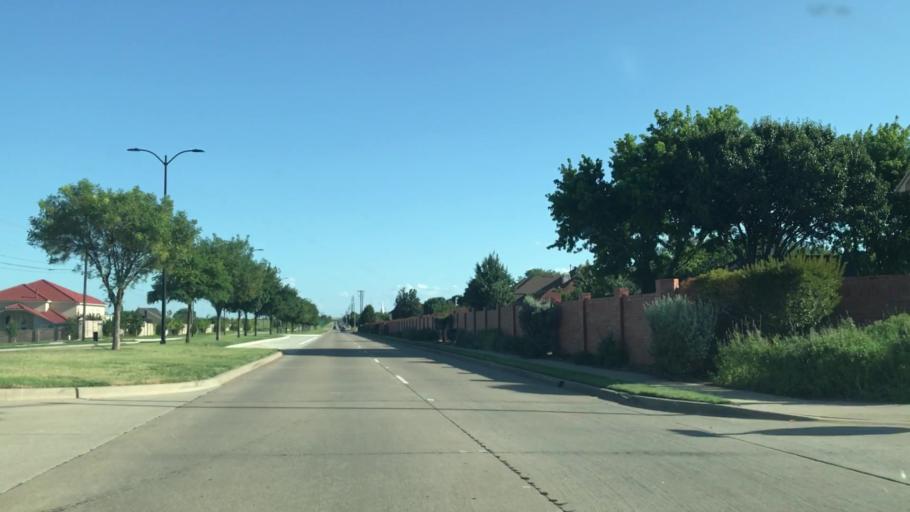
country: US
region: Texas
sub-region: Collin County
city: Frisco
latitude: 33.1268
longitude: -96.7681
